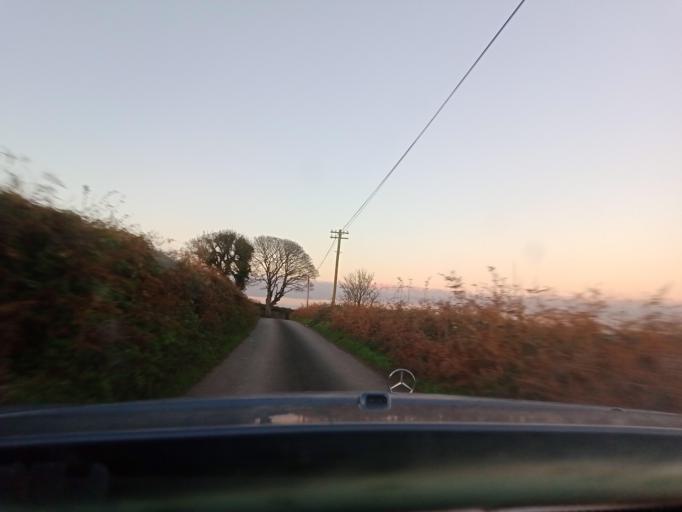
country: IE
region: Leinster
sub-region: Kilkenny
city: Graiguenamanagh
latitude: 52.5585
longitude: -6.9627
